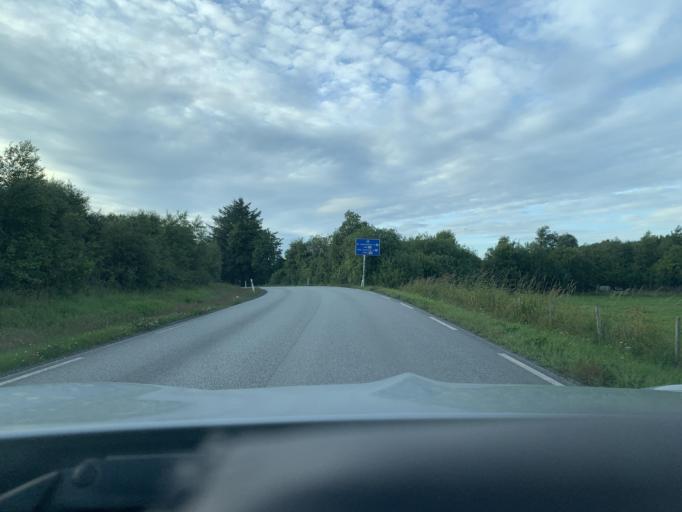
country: NO
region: Rogaland
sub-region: Time
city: Bryne
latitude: 58.6970
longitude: 5.7104
